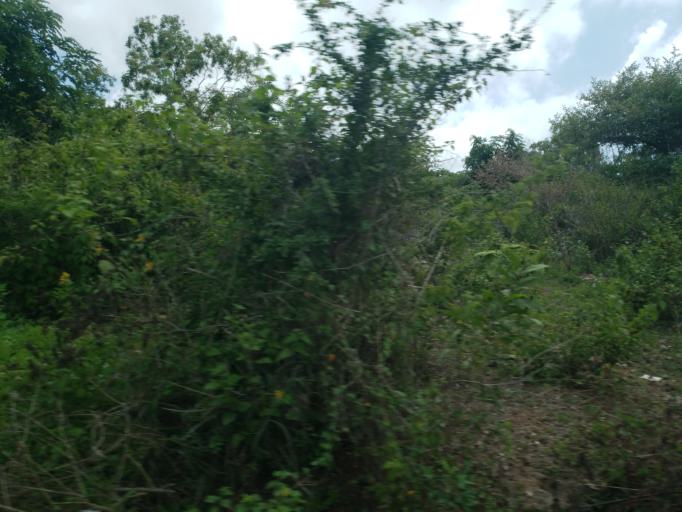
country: ID
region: Bali
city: Kangin
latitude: -8.8284
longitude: 115.1496
